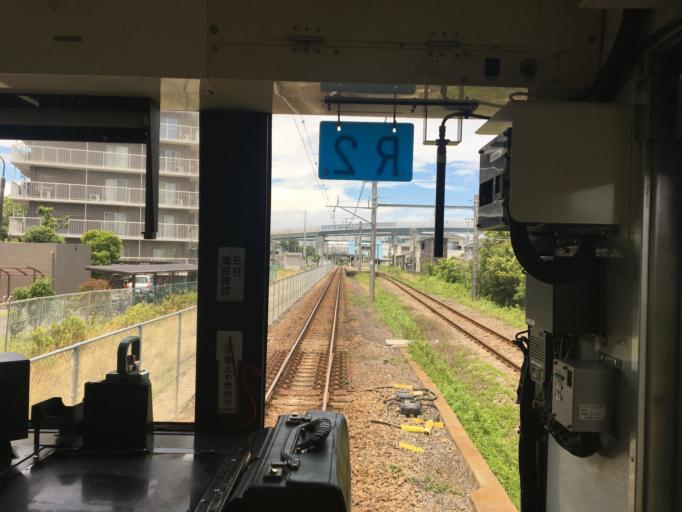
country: JP
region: Kanagawa
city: Atsugi
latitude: 35.4191
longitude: 139.3773
